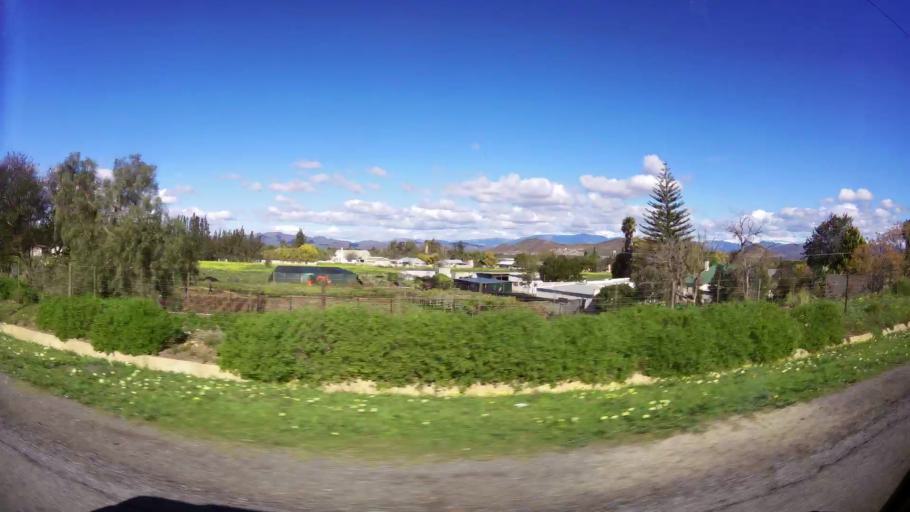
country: ZA
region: Western Cape
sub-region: Cape Winelands District Municipality
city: Ashton
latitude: -33.7956
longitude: 19.8934
